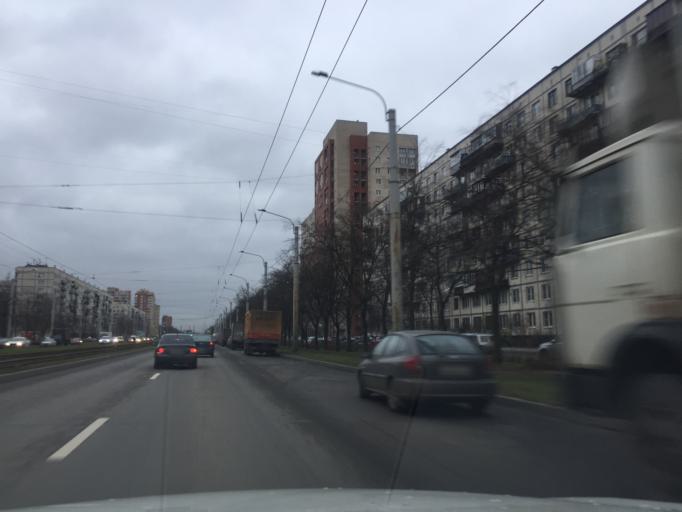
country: RU
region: St.-Petersburg
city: Grazhdanka
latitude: 60.0434
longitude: 30.4016
